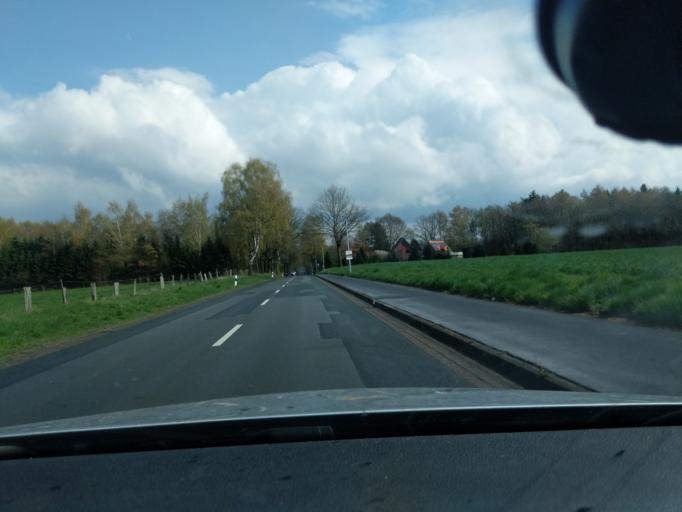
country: DE
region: Lower Saxony
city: Bargstedt
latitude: 53.4642
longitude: 9.4761
